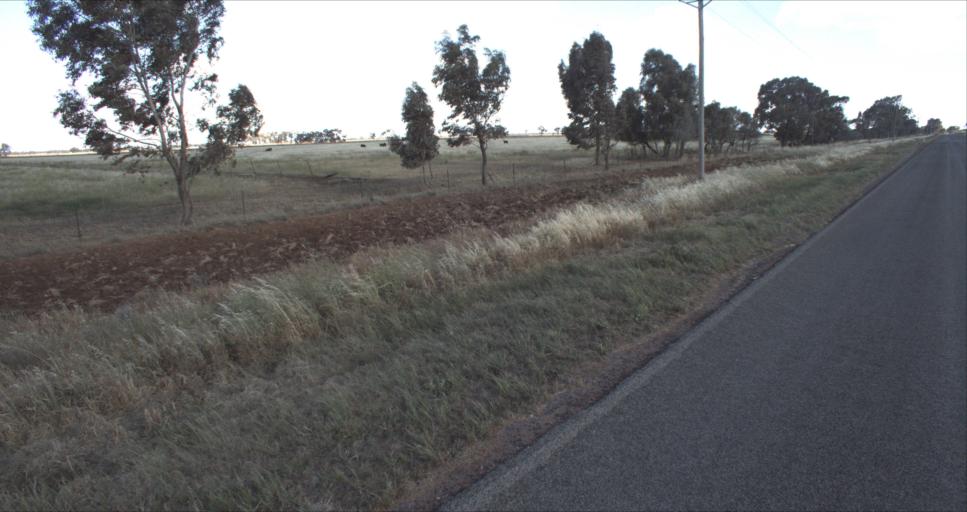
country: AU
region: New South Wales
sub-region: Leeton
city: Leeton
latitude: -34.5322
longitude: 146.2812
